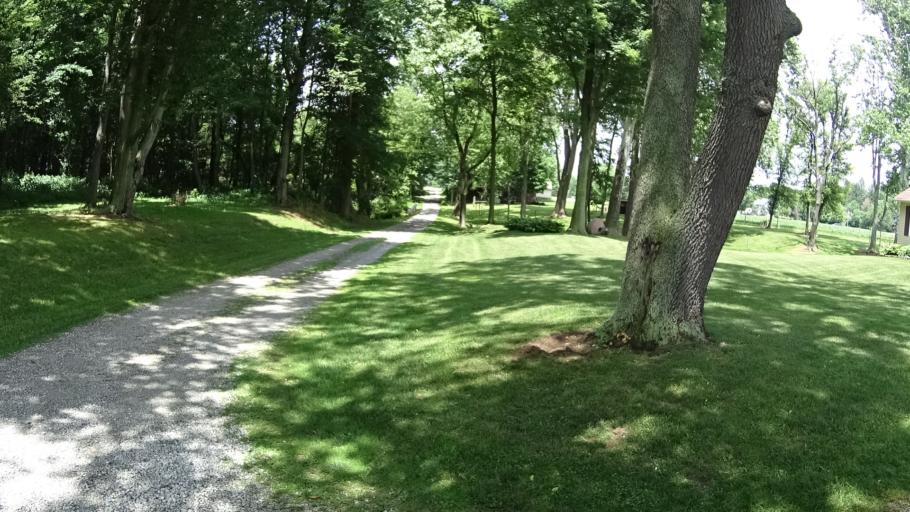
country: US
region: Ohio
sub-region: Erie County
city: Milan
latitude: 41.2971
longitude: -82.5887
